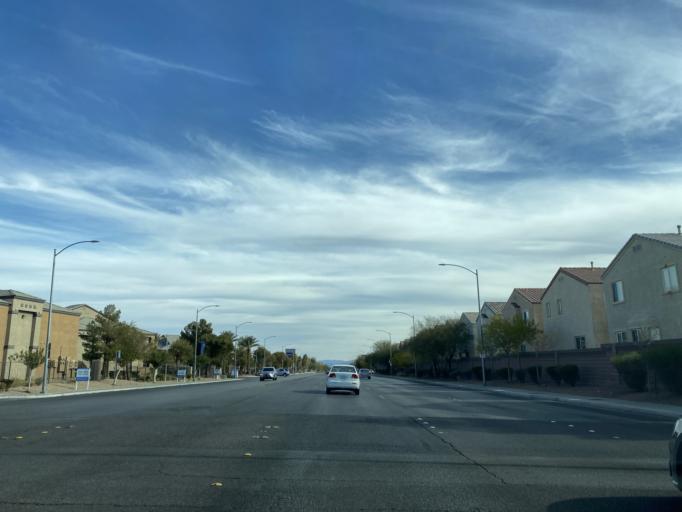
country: US
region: Nevada
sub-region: Clark County
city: Enterprise
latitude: 36.0559
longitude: -115.2388
